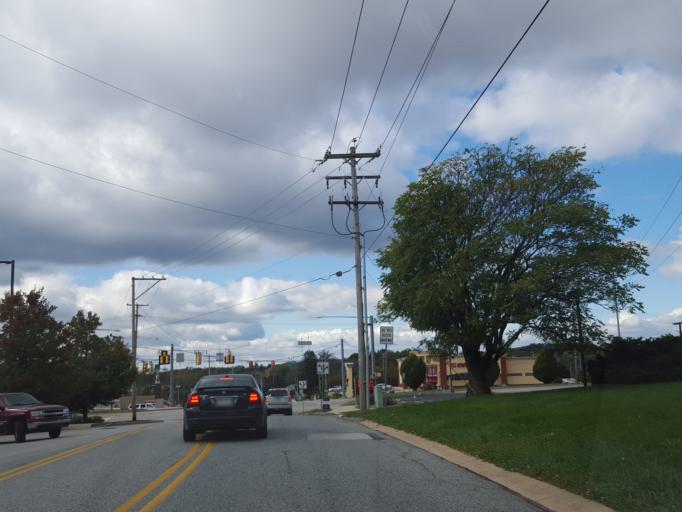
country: US
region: Pennsylvania
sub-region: York County
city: Valley View
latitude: 39.9362
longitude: -76.6912
